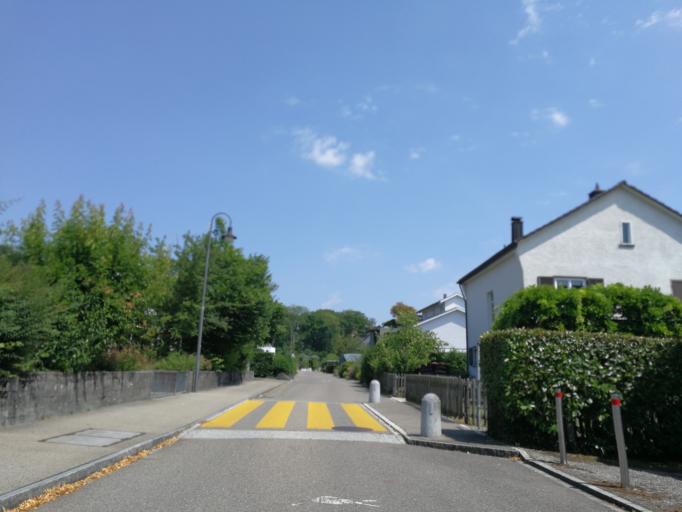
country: CH
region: Zurich
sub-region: Bezirk Meilen
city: Meilen
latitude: 47.2699
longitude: 8.6545
